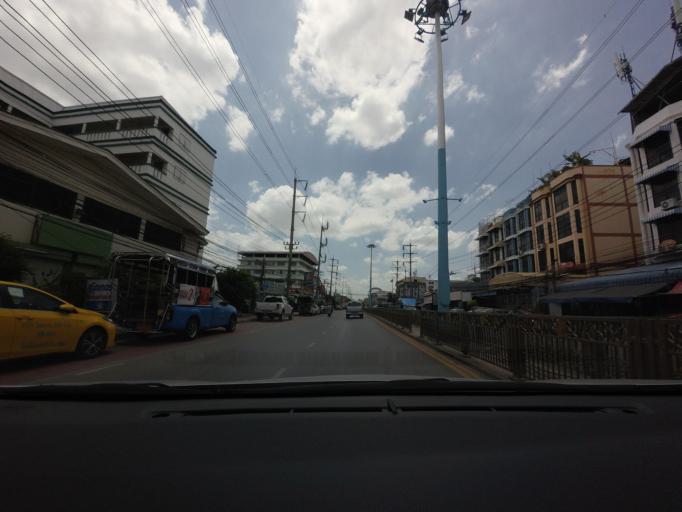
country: TH
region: Samut Prakan
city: Samut Prakan
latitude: 13.5742
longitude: 100.5919
